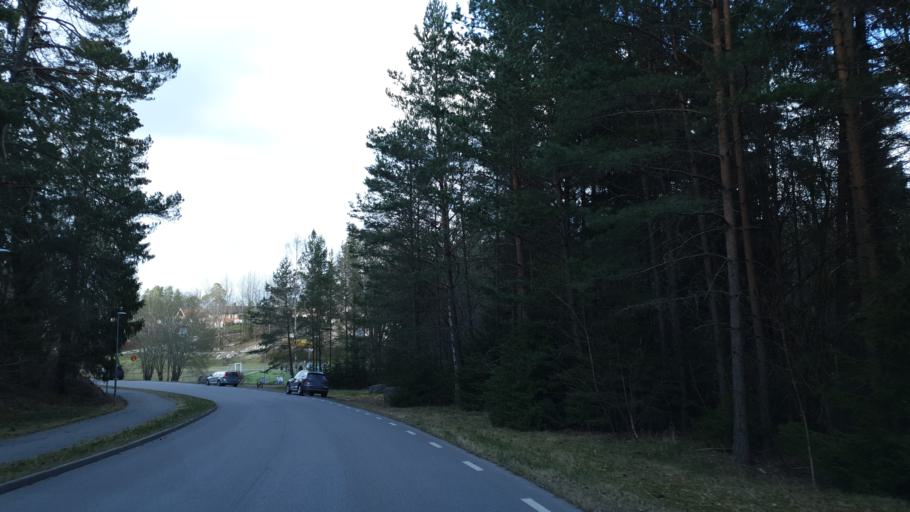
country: SE
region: Stockholm
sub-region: Lidingo
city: Lidingoe
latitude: 59.3872
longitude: 18.1197
